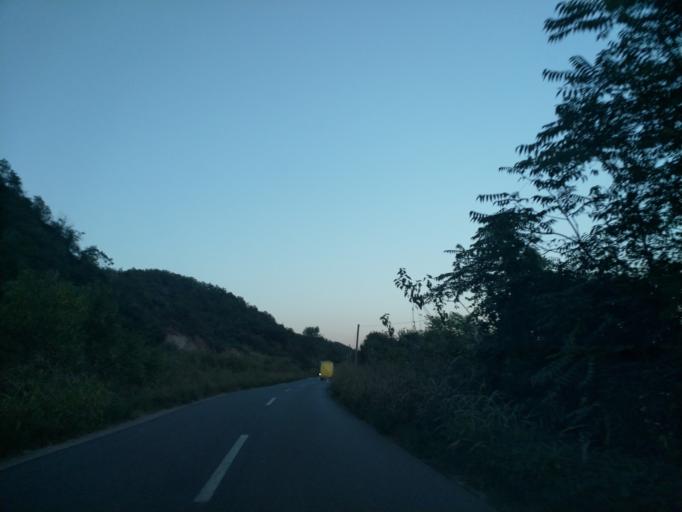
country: RS
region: Central Serbia
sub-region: Rasinski Okrug
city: Krusevac
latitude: 43.6031
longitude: 21.2714
